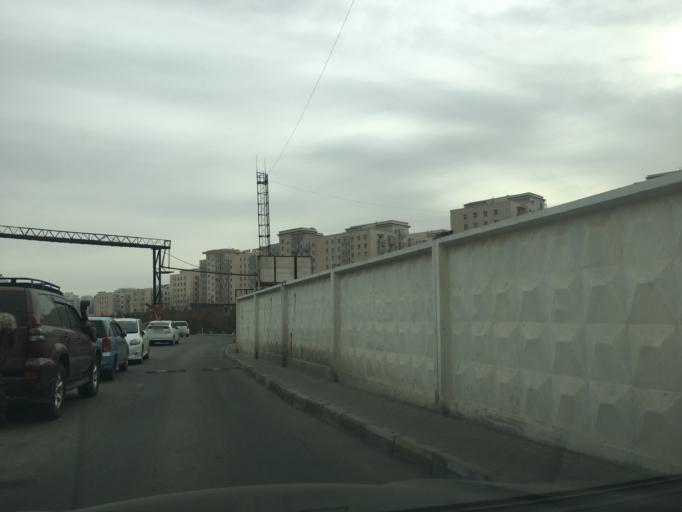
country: MN
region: Ulaanbaatar
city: Ulaanbaatar
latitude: 47.9050
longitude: 106.8873
